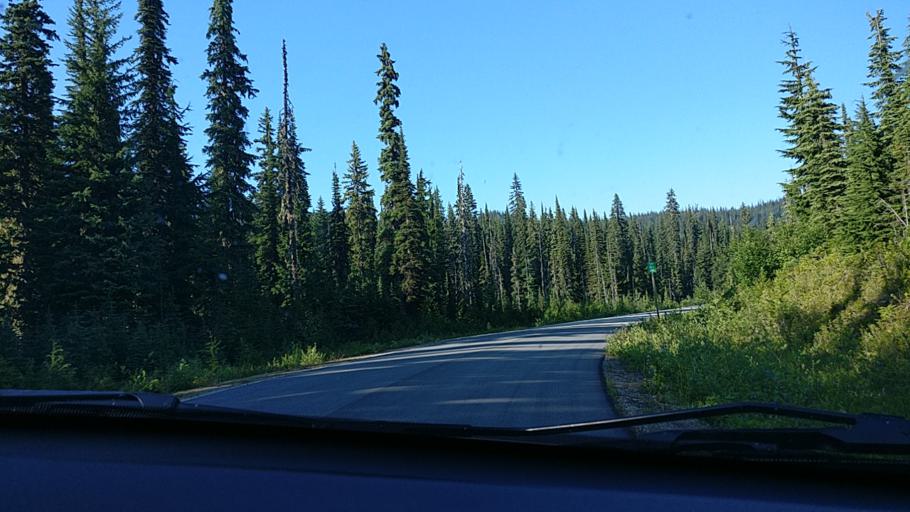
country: CA
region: British Columbia
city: Revelstoke
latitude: 51.0231
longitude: -118.1561
